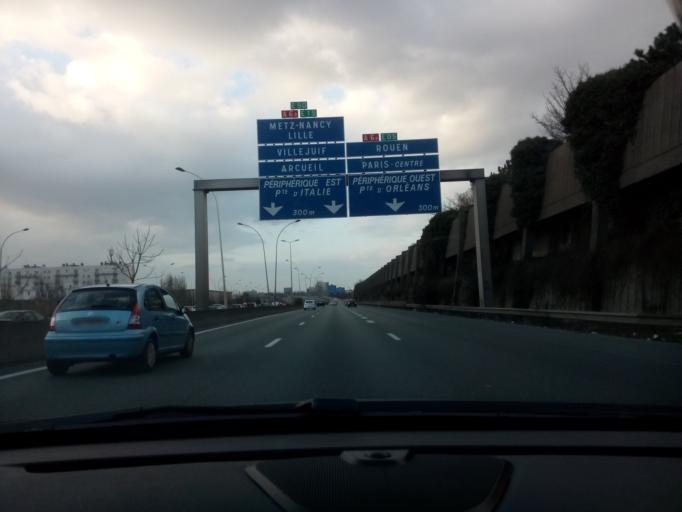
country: FR
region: Ile-de-France
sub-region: Departement du Val-de-Marne
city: Chevilly-Larue
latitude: 48.7756
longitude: 2.3464
